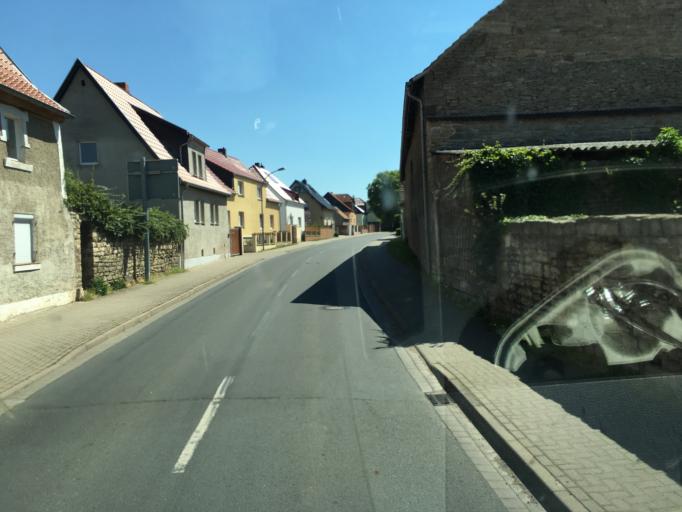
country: DE
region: Thuringia
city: Rossleben
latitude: 51.3040
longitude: 11.4043
